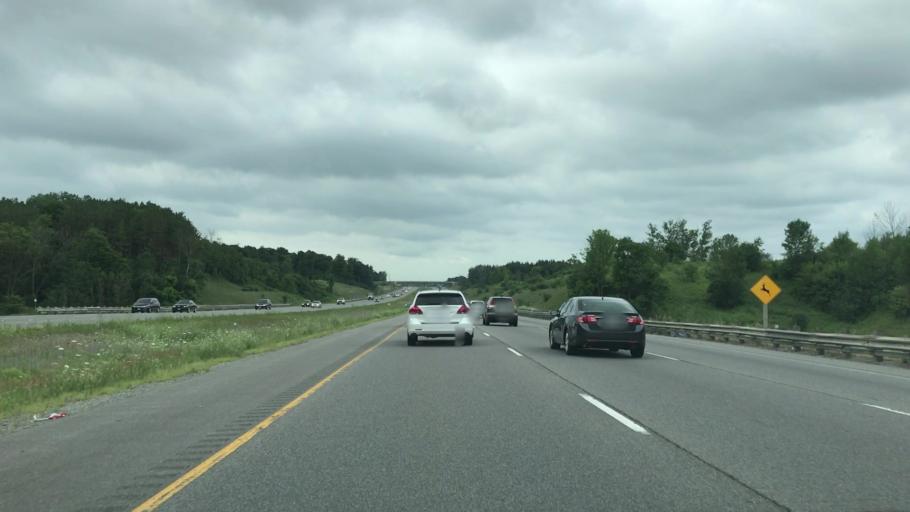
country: CA
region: Ontario
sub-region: York
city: Richmond Hill
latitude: 43.9676
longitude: -79.3928
